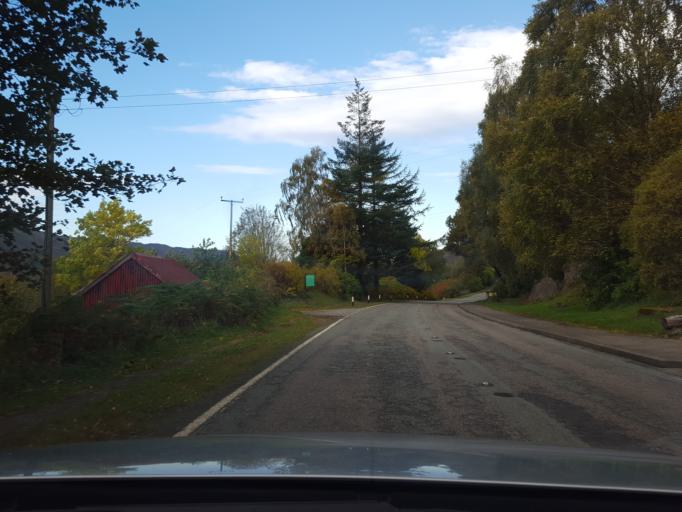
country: GB
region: Scotland
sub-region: Highland
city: Fort William
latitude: 57.2432
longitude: -5.4598
